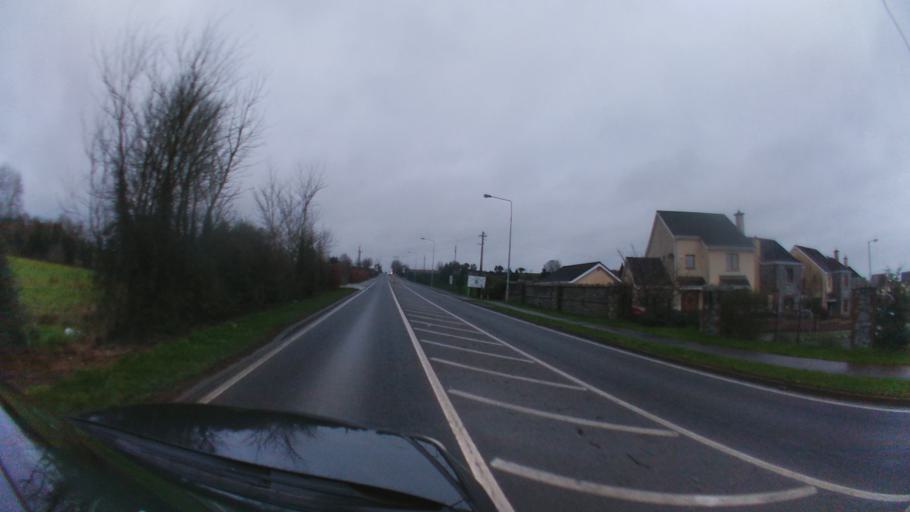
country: IE
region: Leinster
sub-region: Kildare
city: Castledermot
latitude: 52.9056
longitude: -6.8391
